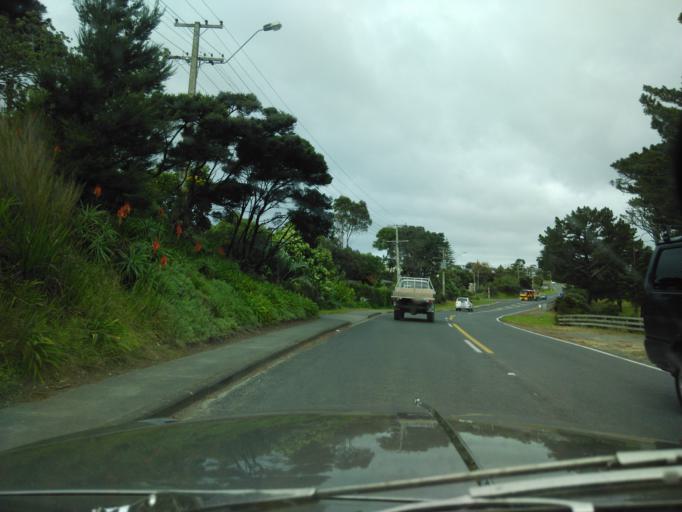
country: NZ
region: Auckland
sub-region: Auckland
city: Wellsford
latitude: -36.0941
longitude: 174.5855
